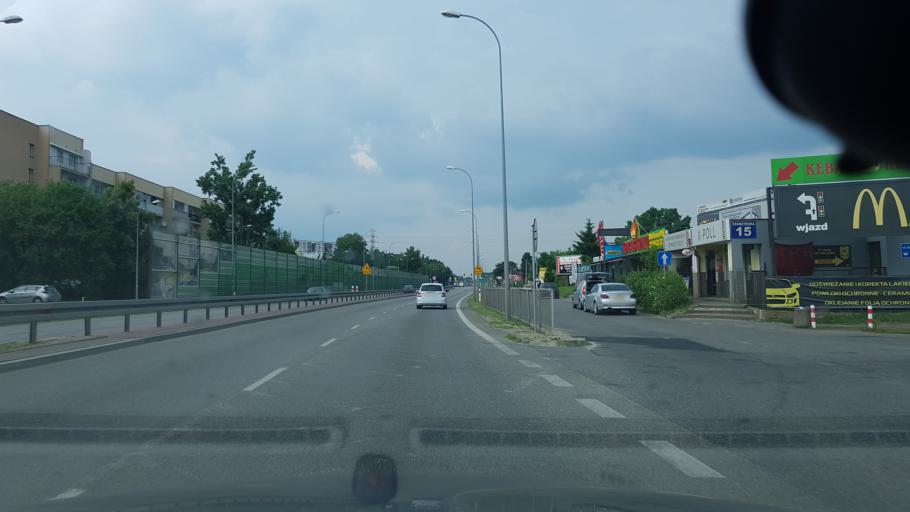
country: PL
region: Masovian Voivodeship
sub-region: Powiat legionowski
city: Jablonna
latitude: 52.3853
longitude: 20.9259
